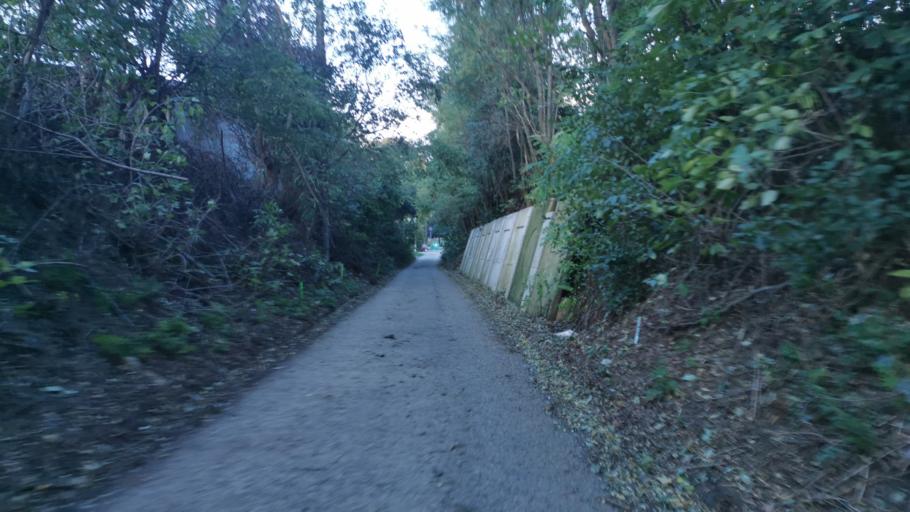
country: SK
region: Trnavsky
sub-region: Okres Skalica
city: Skalica
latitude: 48.8106
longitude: 17.2440
